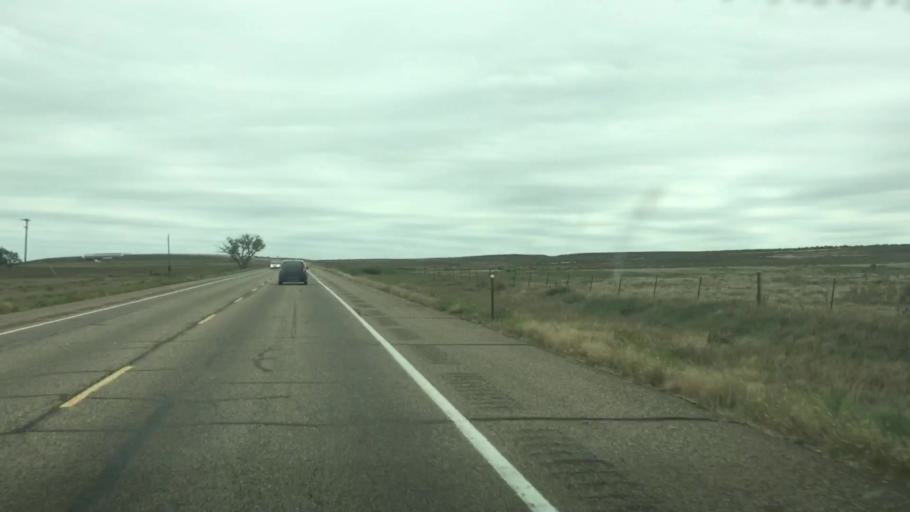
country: US
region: Colorado
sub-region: Prowers County
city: Lamar
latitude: 38.0519
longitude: -102.2697
